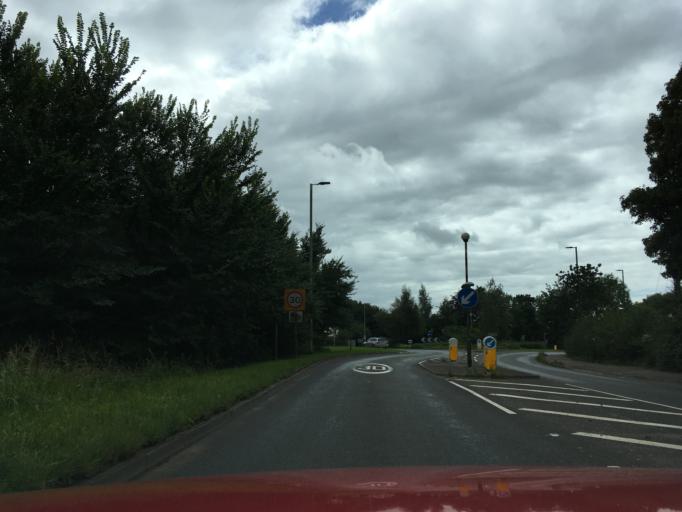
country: GB
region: England
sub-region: Devon
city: Uffculme
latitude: 50.8942
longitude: -3.3674
